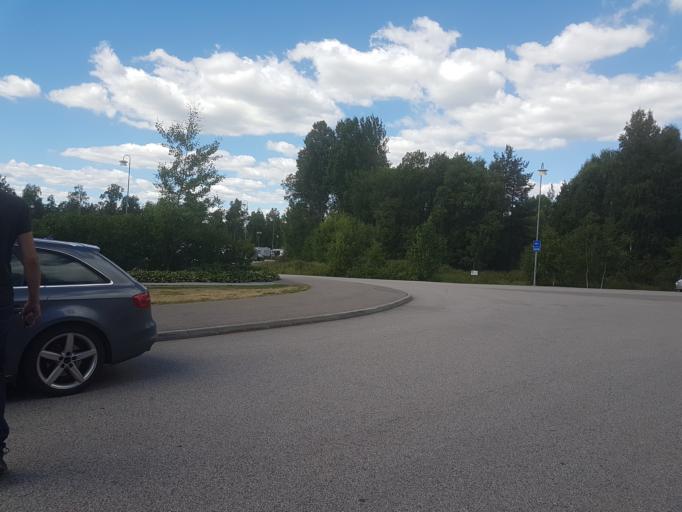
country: SE
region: Kronoberg
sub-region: Lessebo Kommun
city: Lessebo
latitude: 56.8498
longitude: 15.3920
